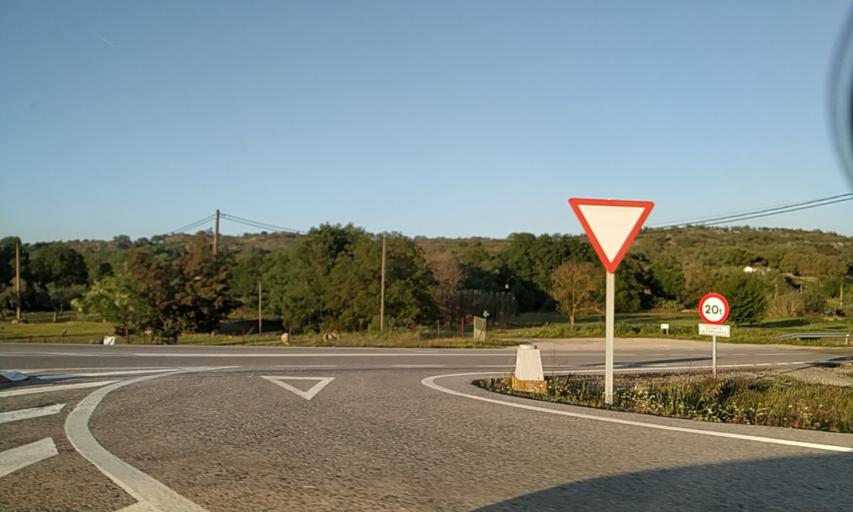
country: ES
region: Extremadura
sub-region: Provincia de Caceres
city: Valencia de Alcantara
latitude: 39.3936
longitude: -7.2463
